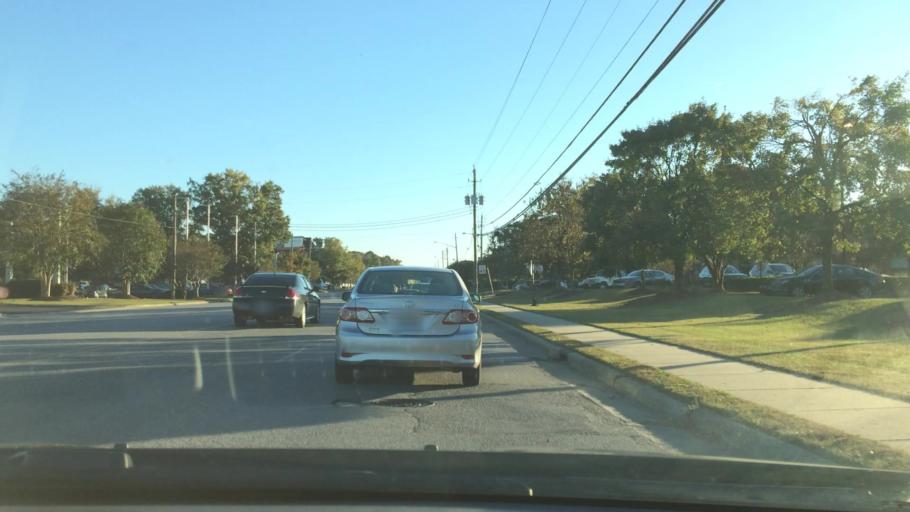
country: US
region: North Carolina
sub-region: Pitt County
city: Summerfield
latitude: 35.5806
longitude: -77.3810
